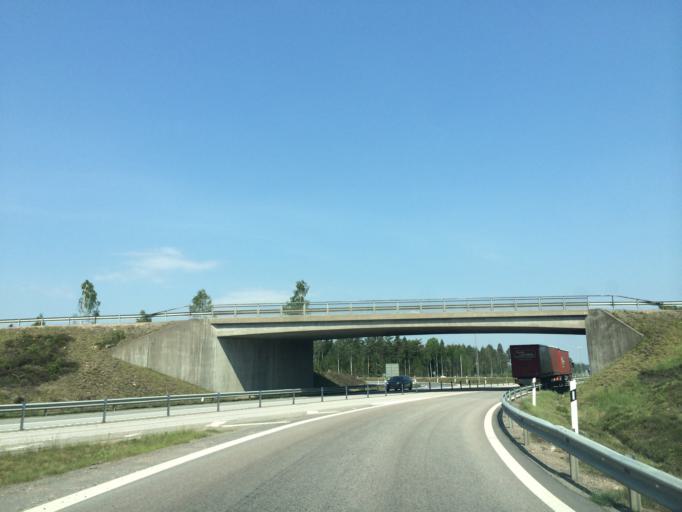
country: SE
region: Kronoberg
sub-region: Ljungby Kommun
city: Ljungby
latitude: 56.8119
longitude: 13.9029
